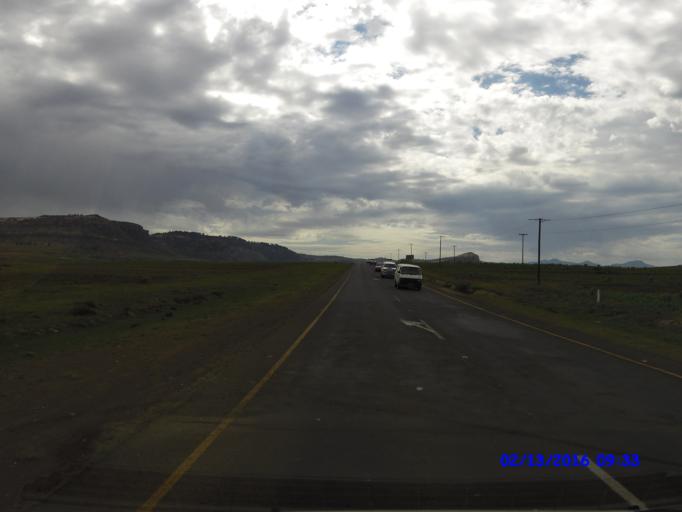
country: LS
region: Maseru
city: Maseru
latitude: -29.4201
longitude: 27.6475
